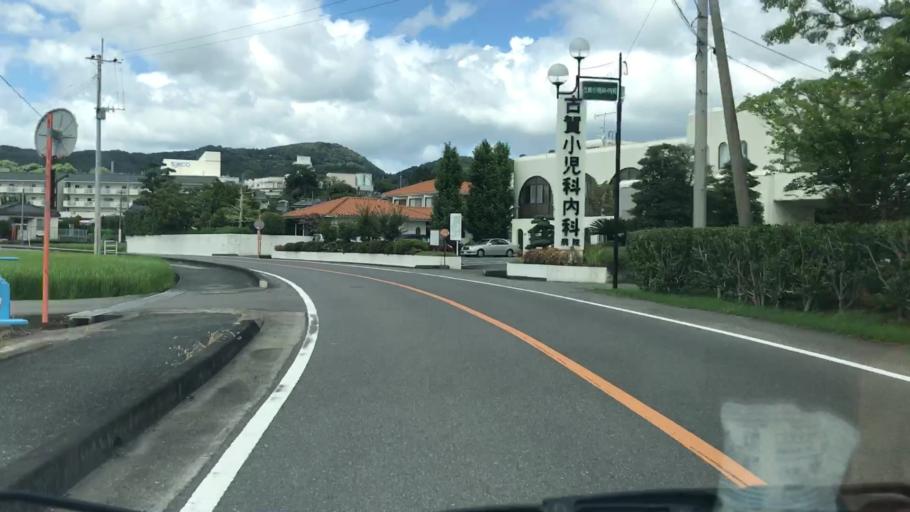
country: JP
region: Saga Prefecture
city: Takeocho-takeo
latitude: 33.2254
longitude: 130.1450
